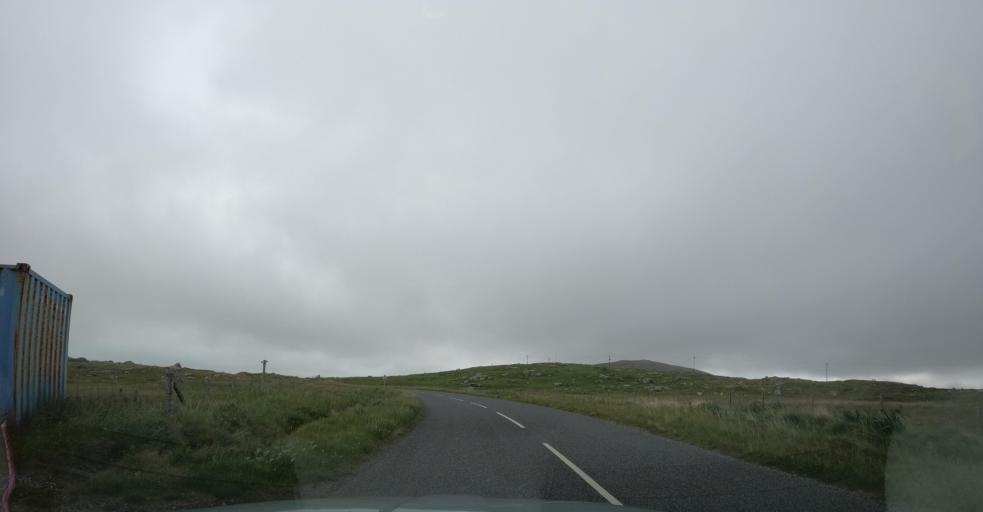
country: GB
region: Scotland
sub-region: Eilean Siar
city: Isle of North Uist
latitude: 57.6643
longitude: -7.2334
